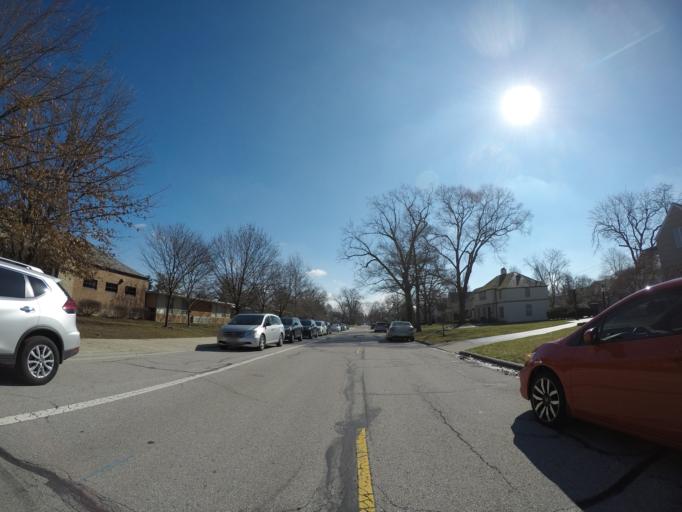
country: US
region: Ohio
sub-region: Franklin County
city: Upper Arlington
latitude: 40.0000
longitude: -83.0561
